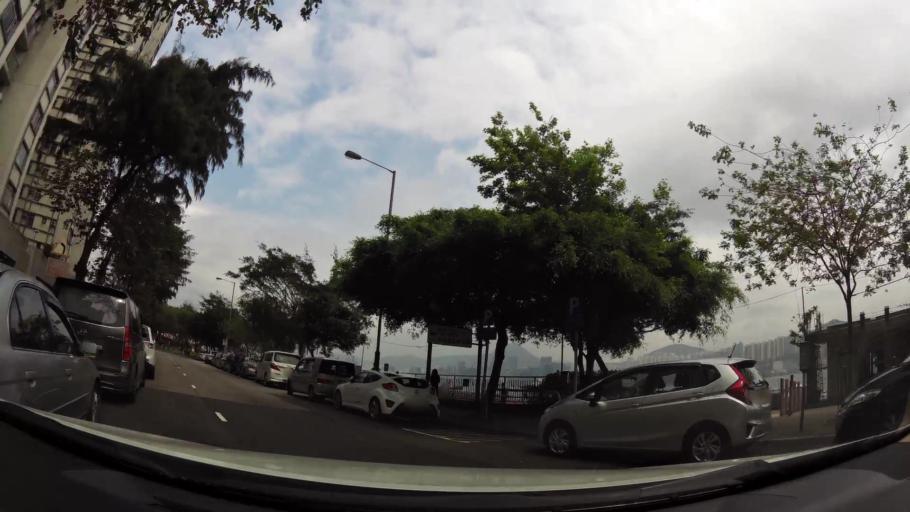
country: HK
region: Kowloon City
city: Kowloon
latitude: 22.2871
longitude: 114.2230
